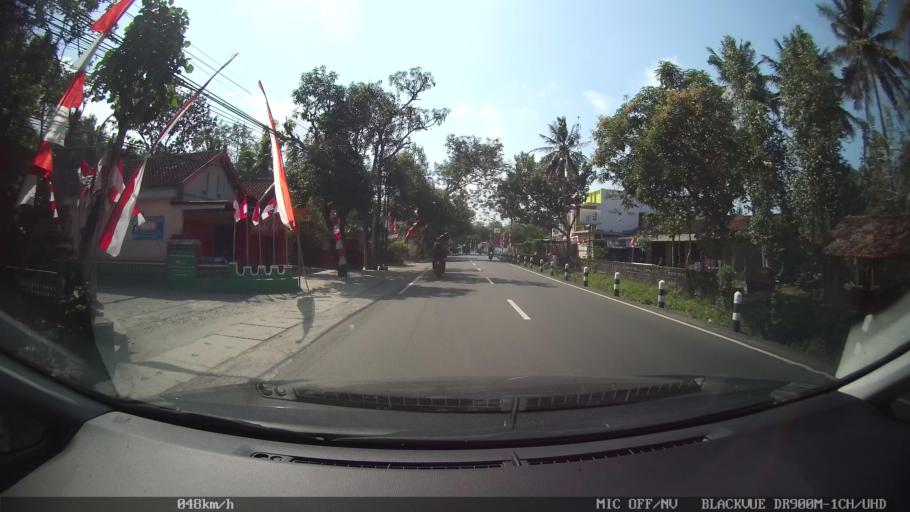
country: ID
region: Daerah Istimewa Yogyakarta
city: Srandakan
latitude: -7.9395
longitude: 110.2263
